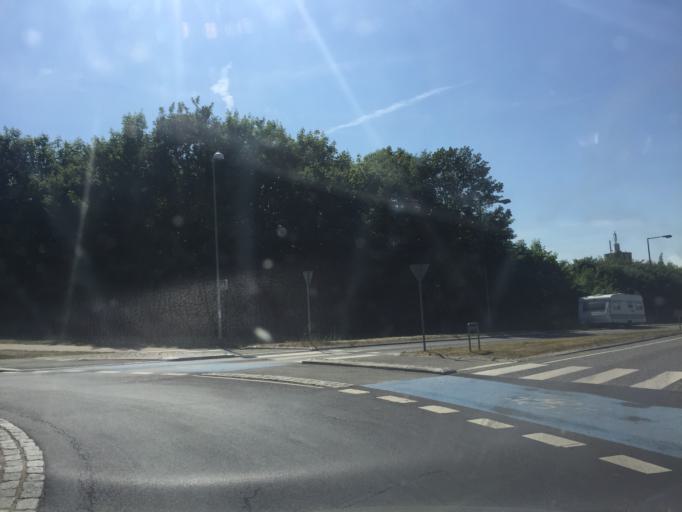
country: DK
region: Capital Region
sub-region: Ballerup Kommune
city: Malov
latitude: 55.7852
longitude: 12.3281
